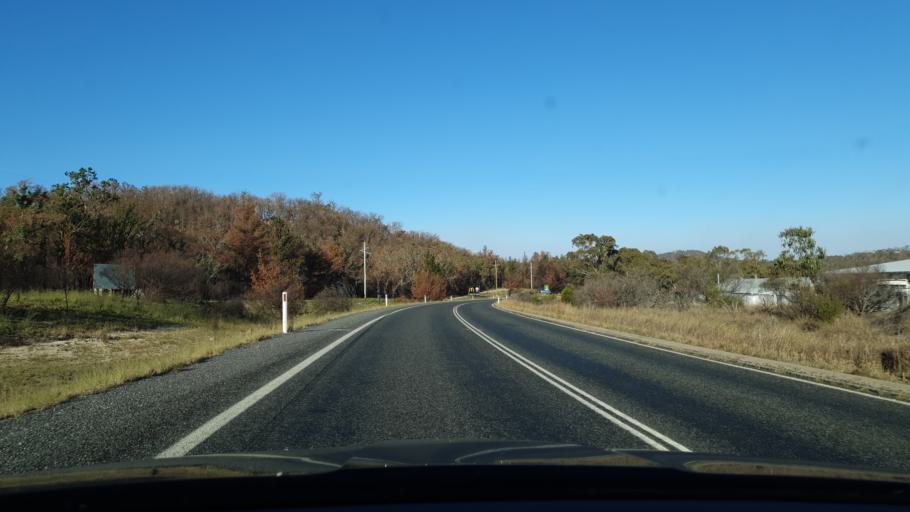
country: AU
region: Queensland
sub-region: Southern Downs
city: Stanthorpe
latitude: -28.6450
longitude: 151.9274
